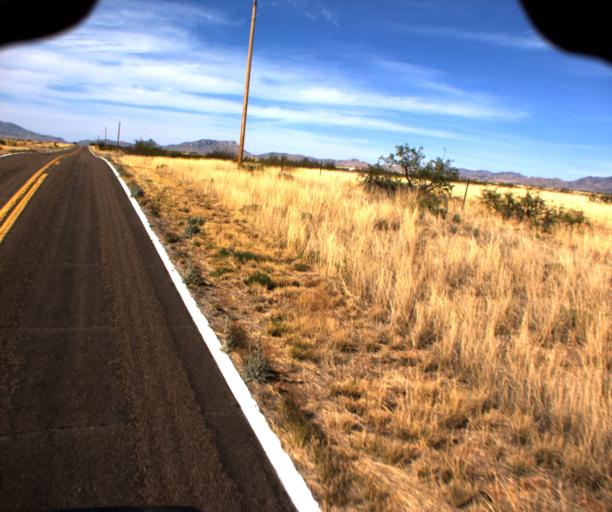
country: US
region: Arizona
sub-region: Cochise County
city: Willcox
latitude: 31.9582
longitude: -109.4772
